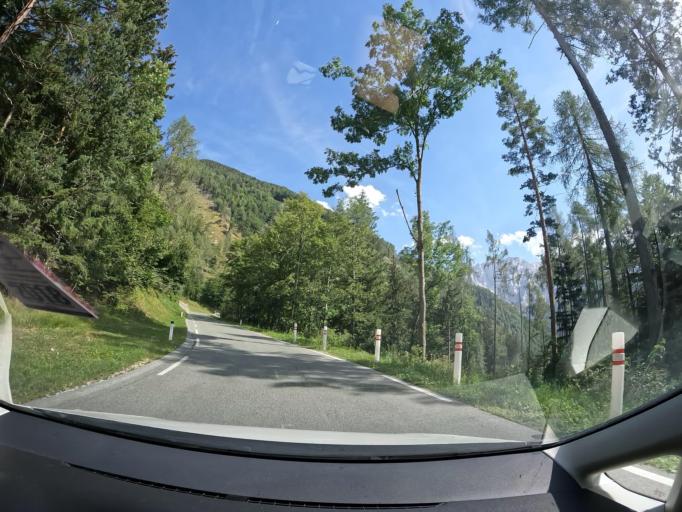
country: AT
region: Carinthia
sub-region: Politischer Bezirk Feldkirchen
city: Glanegg
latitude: 46.7246
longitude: 14.2398
